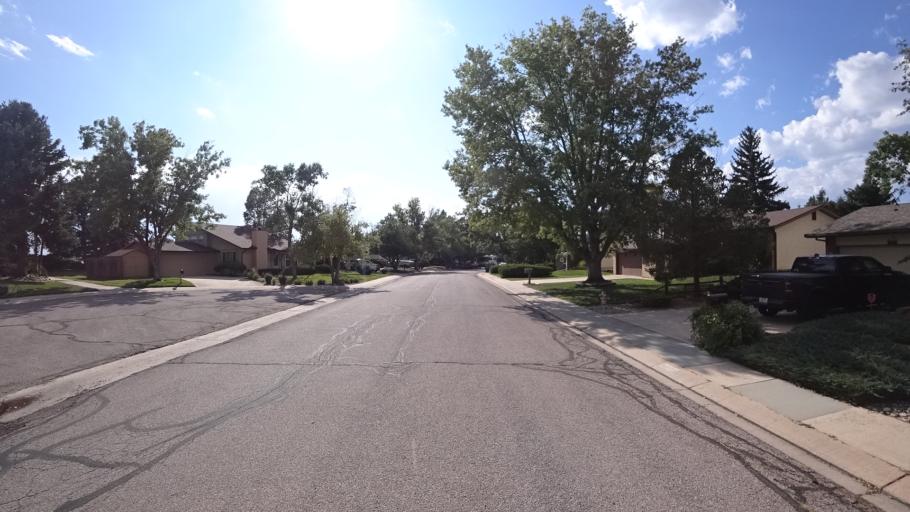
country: US
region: Colorado
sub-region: El Paso County
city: Cimarron Hills
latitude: 38.8716
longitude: -104.7348
